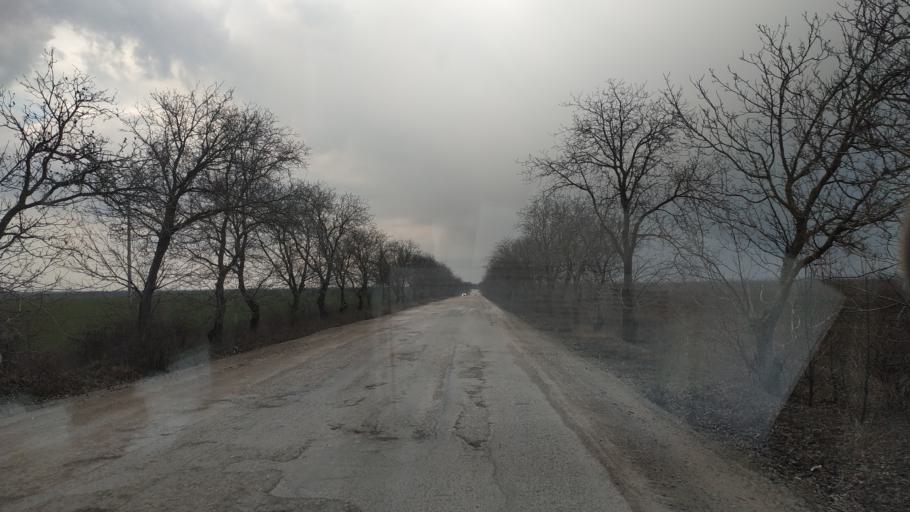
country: MD
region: Telenesti
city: Grigoriopol
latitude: 47.0338
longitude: 29.2927
